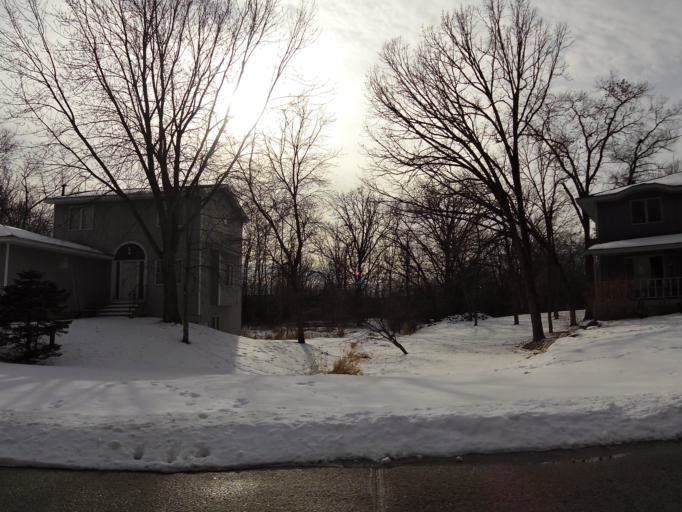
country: US
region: Minnesota
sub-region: Dakota County
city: Lakeville
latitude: 44.6873
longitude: -93.2903
